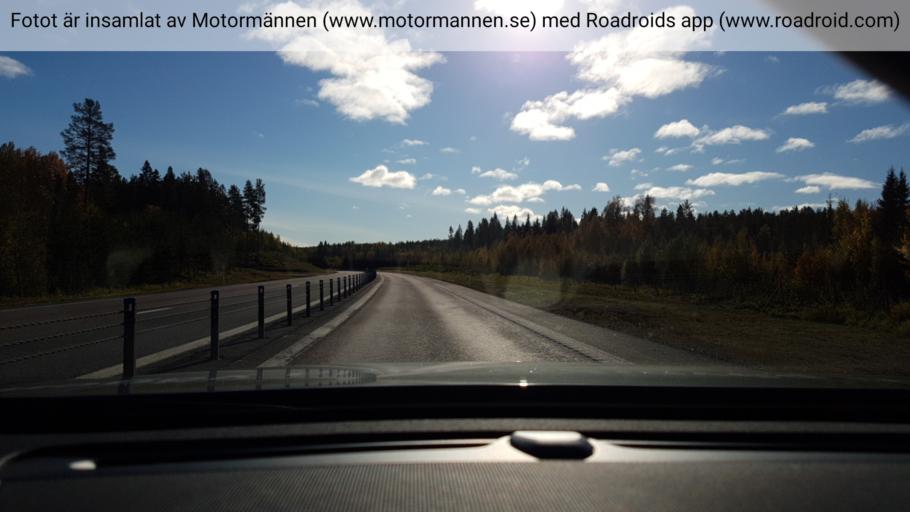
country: SE
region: Vaesterbotten
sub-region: Skelleftea Kommun
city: Skelleftea
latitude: 64.7004
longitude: 21.0050
